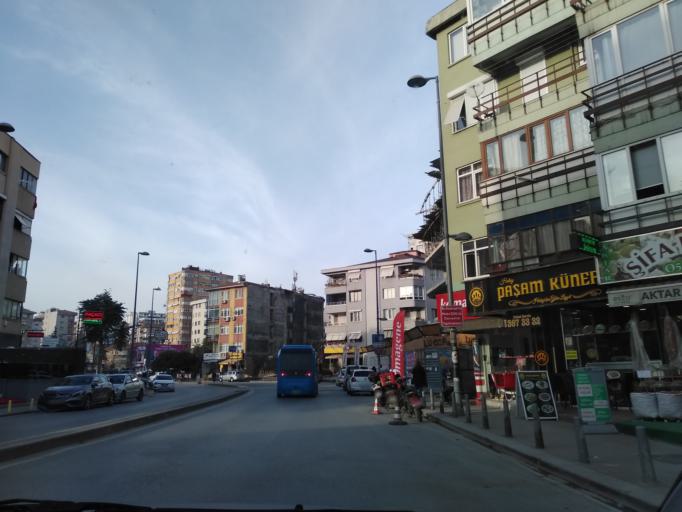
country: TR
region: Istanbul
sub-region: Atasehir
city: Atasehir
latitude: 40.9547
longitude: 29.1008
